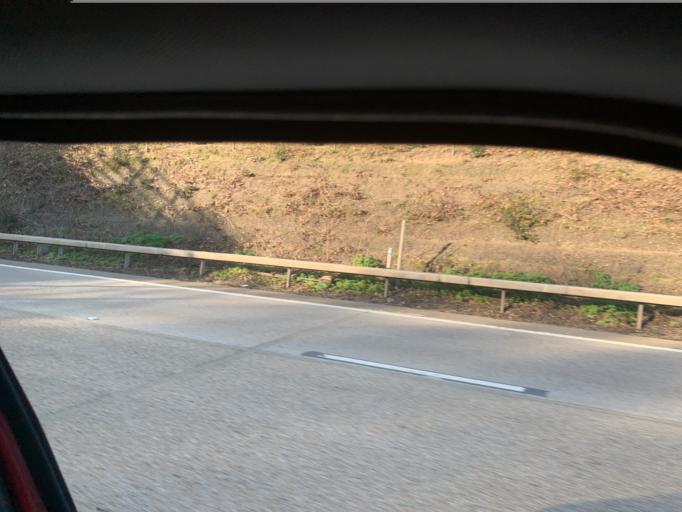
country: GB
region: England
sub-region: Surrey
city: Byfleet
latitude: 51.3243
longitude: -0.4596
